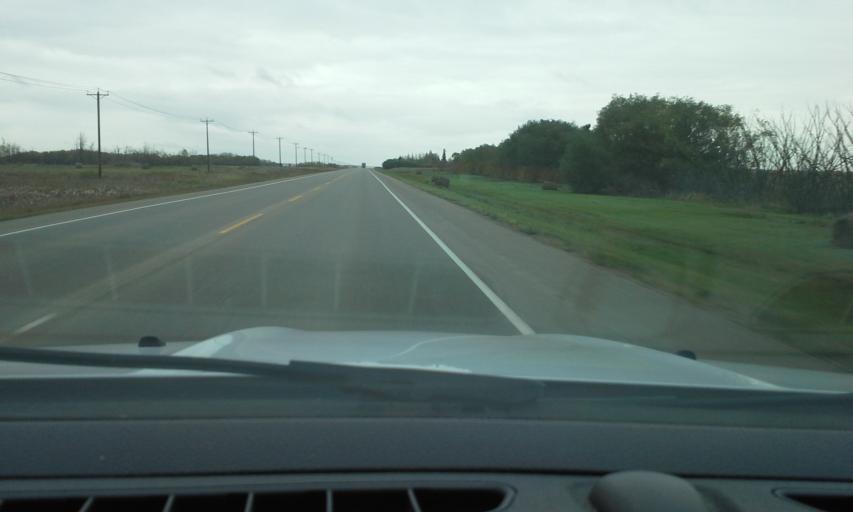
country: CA
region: Saskatchewan
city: Lloydminster
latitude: 53.2780
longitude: -109.8383
